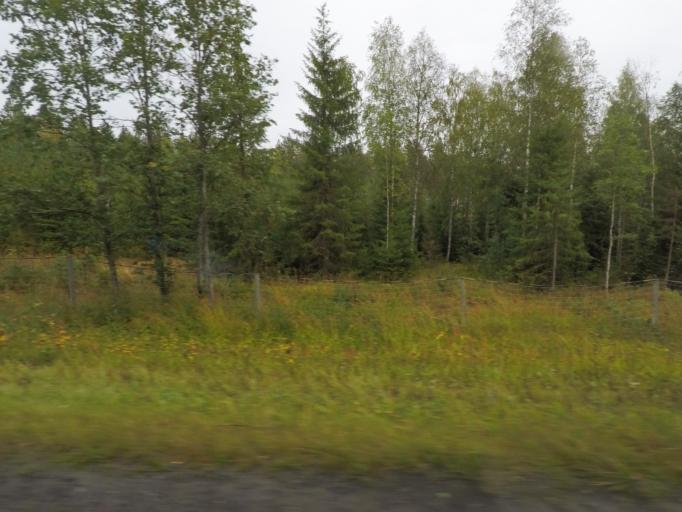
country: FI
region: Southern Savonia
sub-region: Pieksaemaeki
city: Juva
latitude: 61.9847
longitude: 27.8033
